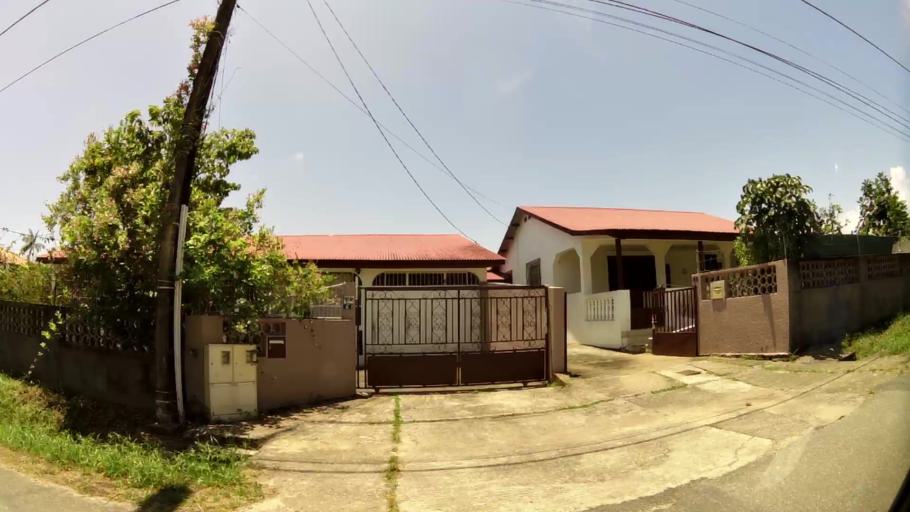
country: GF
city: Macouria
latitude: 4.8881
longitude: -52.3405
